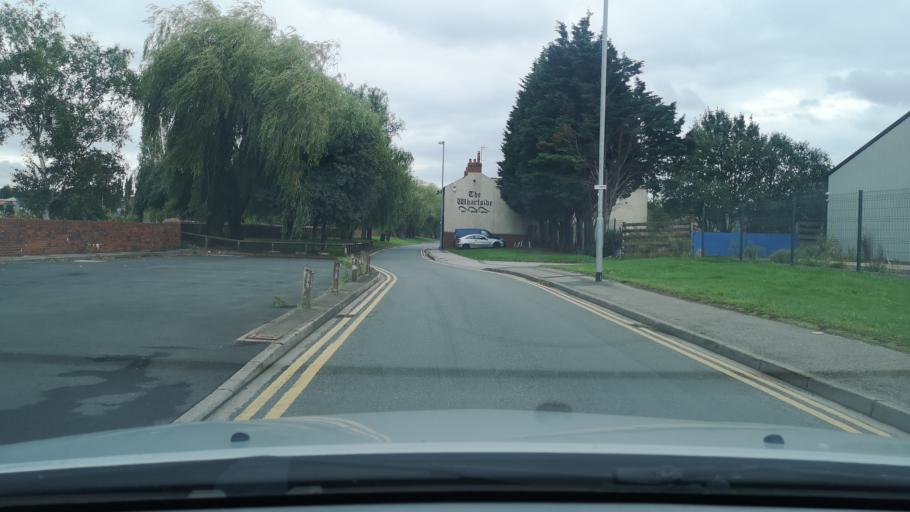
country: GB
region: England
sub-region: City and Borough of Wakefield
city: Wakefield
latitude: 53.6745
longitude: -1.4929
